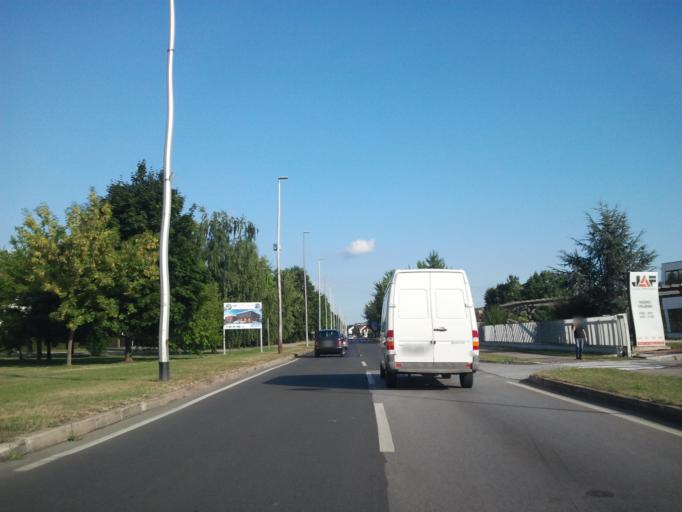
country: HR
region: Zagrebacka
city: Gradici
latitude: 45.7187
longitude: 16.0550
